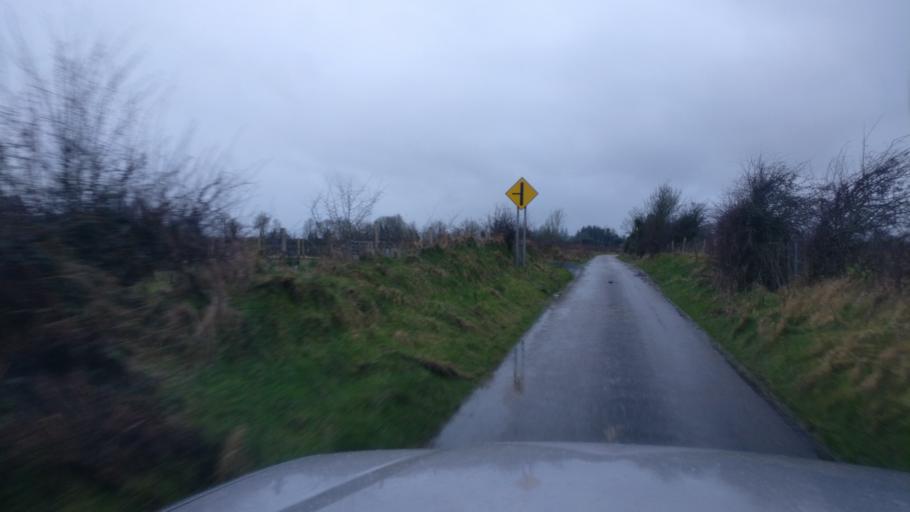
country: IE
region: Connaught
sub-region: County Galway
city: Ballinasloe
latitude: 53.2753
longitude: -8.3319
